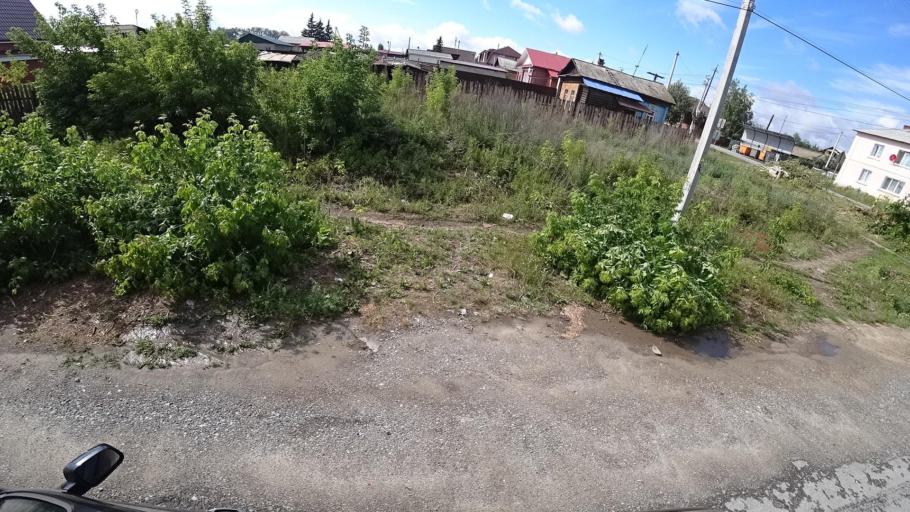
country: RU
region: Sverdlovsk
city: Kamyshlov
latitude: 56.8387
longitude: 62.7103
